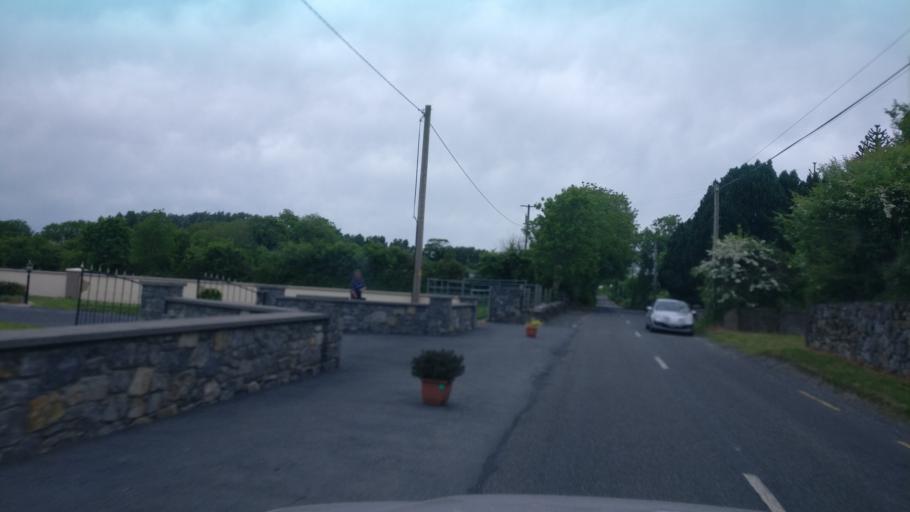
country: IE
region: Connaught
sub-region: County Galway
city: Portumna
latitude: 53.1017
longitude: -8.2526
